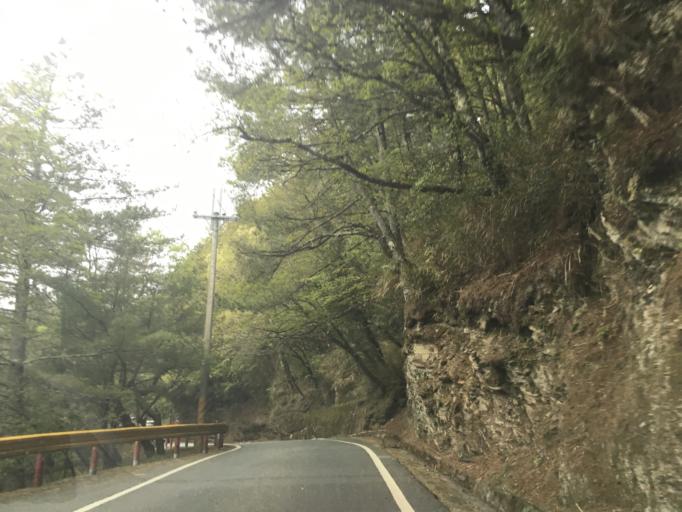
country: TW
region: Taiwan
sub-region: Hualien
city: Hualian
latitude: 24.1807
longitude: 121.3222
